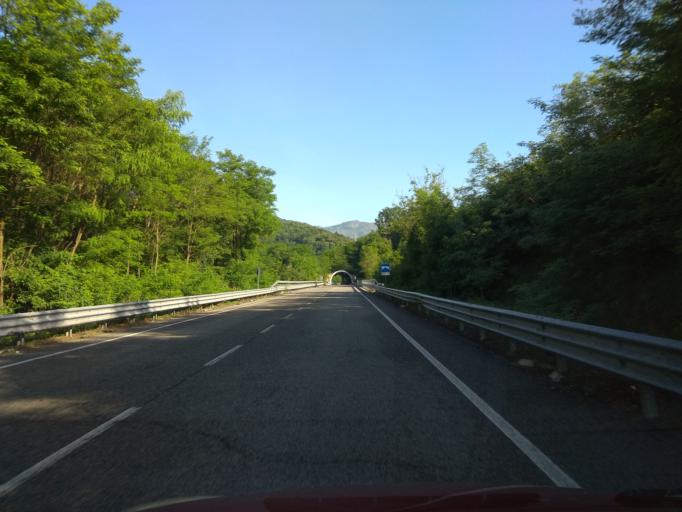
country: IT
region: Piedmont
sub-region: Provincia di Biella
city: Vallanzengo
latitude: 45.6103
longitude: 8.1594
